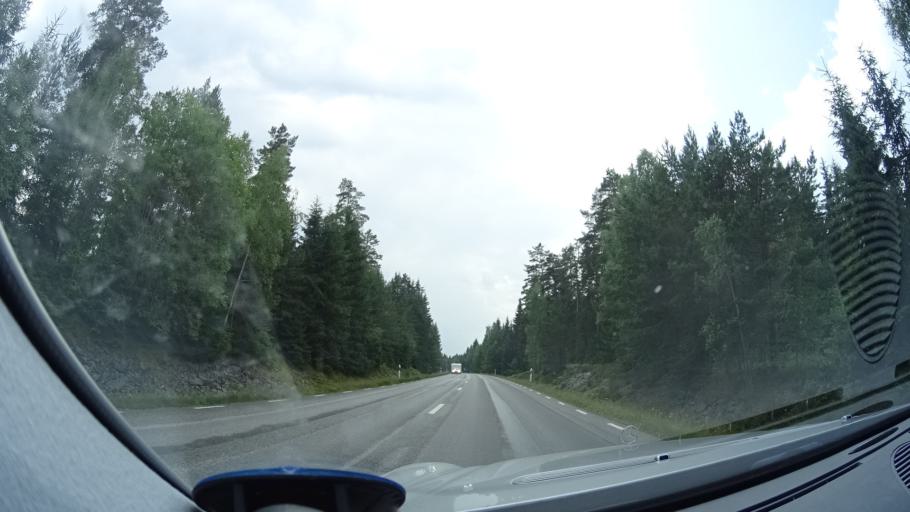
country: SE
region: Kalmar
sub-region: Nybro Kommun
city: Nybro
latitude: 56.7066
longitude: 15.7294
